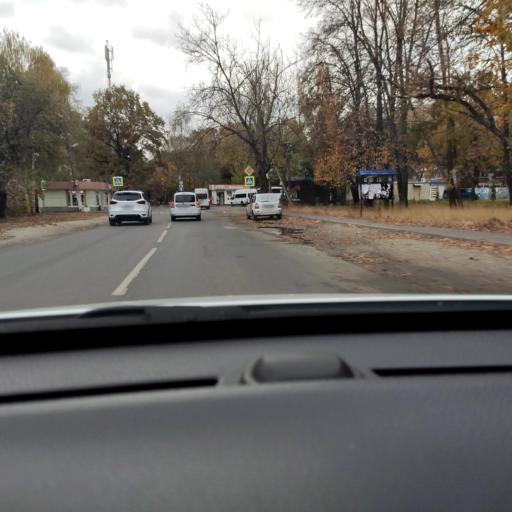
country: RU
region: Voronezj
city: Voronezh
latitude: 51.7224
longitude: 39.2174
